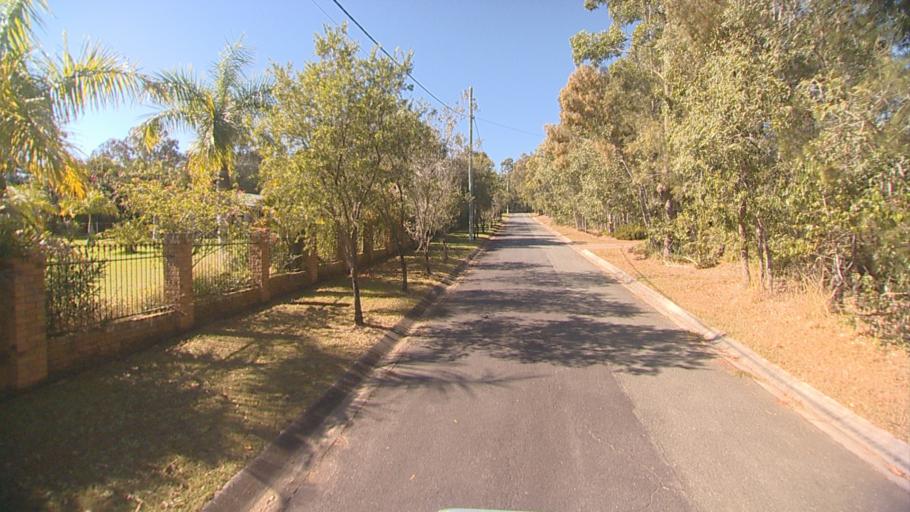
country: AU
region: Queensland
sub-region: Logan
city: Park Ridge South
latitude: -27.6987
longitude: 153.0060
